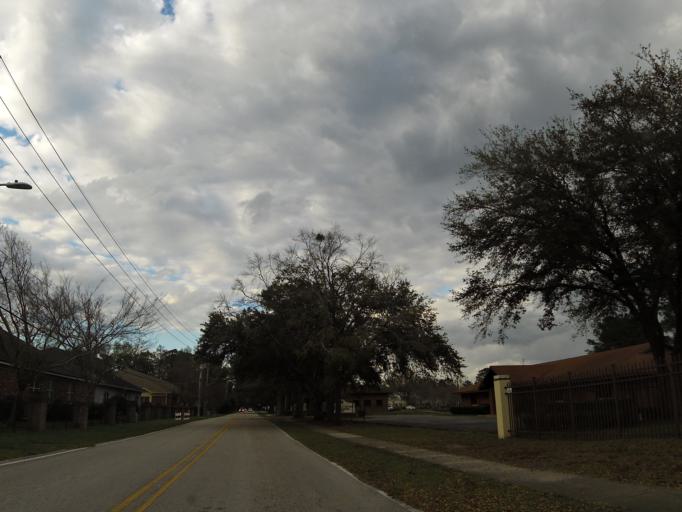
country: US
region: Florida
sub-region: Duval County
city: Jacksonville
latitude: 30.2559
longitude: -81.6219
